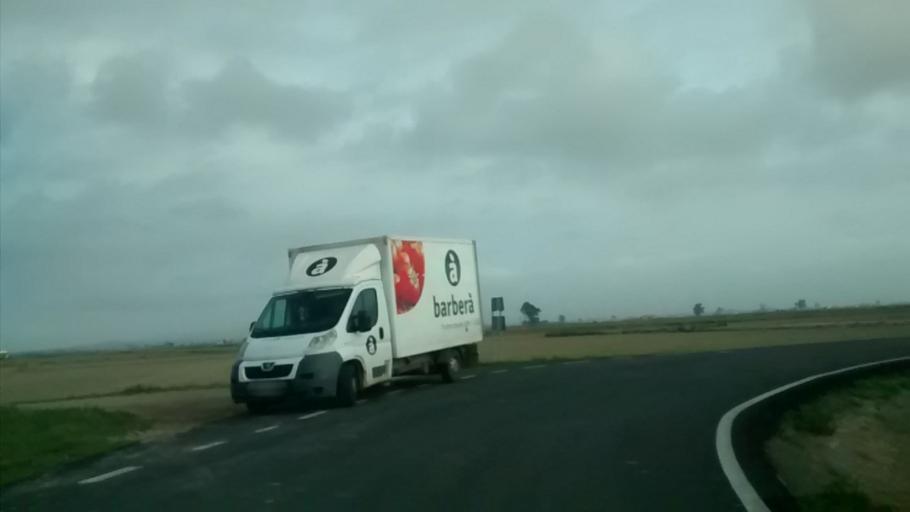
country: ES
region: Catalonia
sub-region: Provincia de Tarragona
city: Deltebre
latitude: 40.6716
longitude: 0.6511
